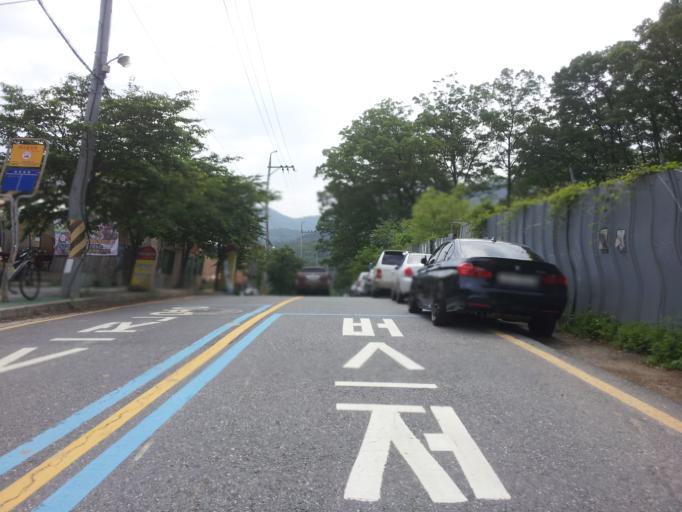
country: KR
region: Daejeon
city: Daejeon
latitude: 36.3308
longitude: 127.4812
